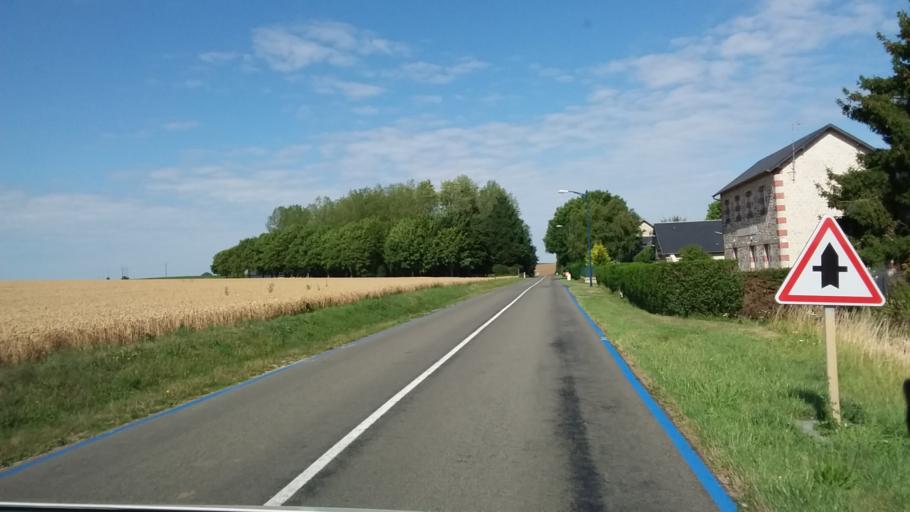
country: FR
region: Picardie
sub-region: Departement de l'Aisne
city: Vailly-sur-Aisne
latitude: 49.4471
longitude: 3.5586
